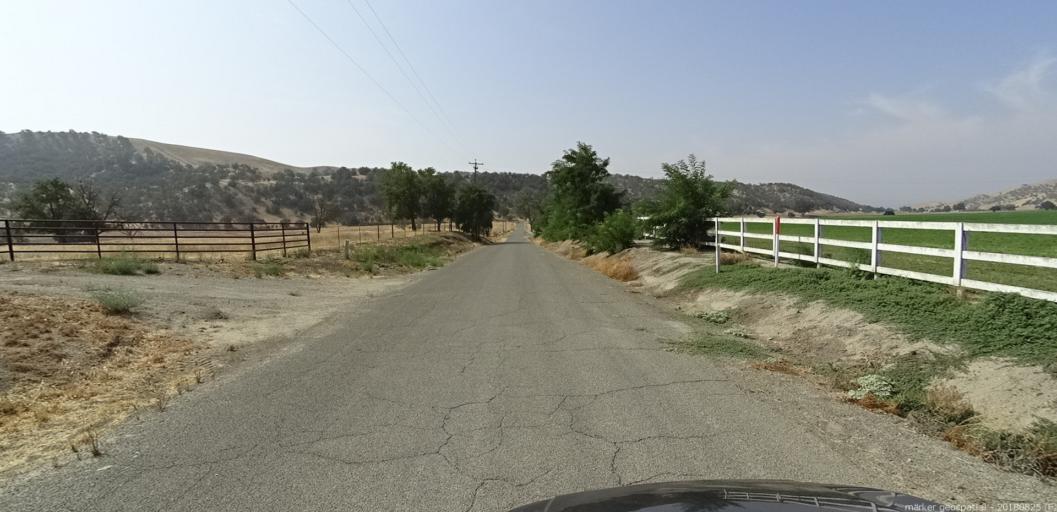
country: US
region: California
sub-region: San Luis Obispo County
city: San Miguel
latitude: 35.8257
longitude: -120.6554
